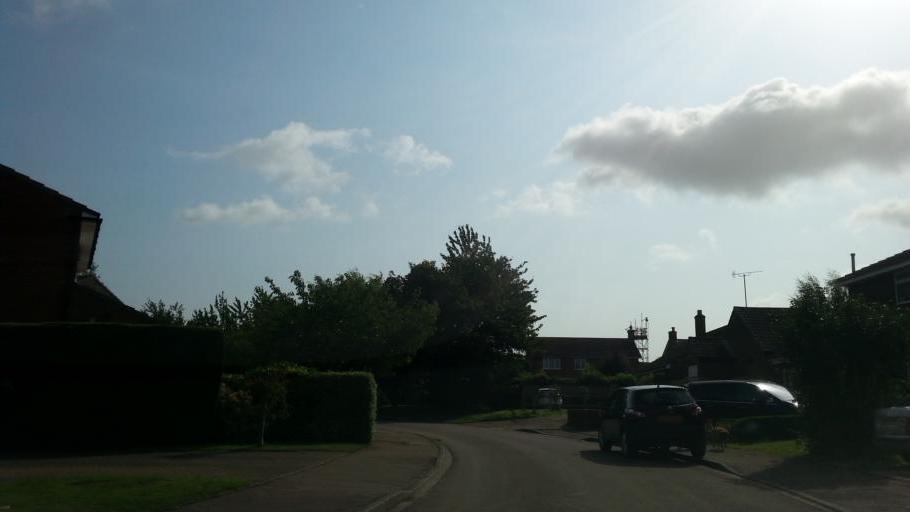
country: GB
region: England
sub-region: Cambridgeshire
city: Comberton
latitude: 52.2147
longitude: 0.0045
